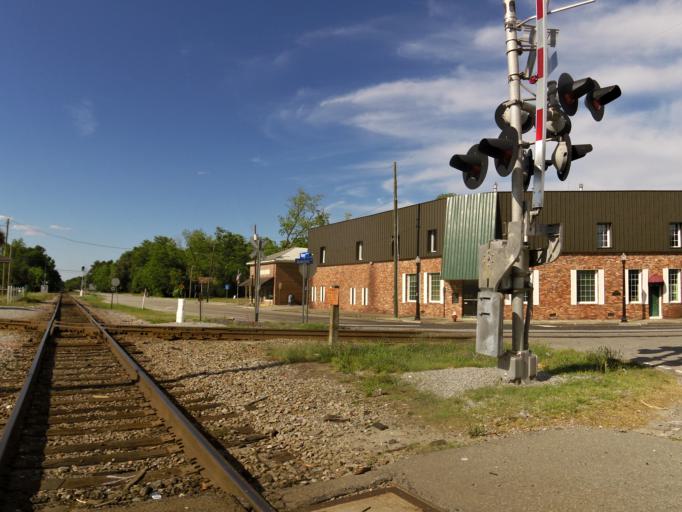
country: US
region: South Carolina
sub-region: Allendale County
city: Fairfax
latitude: 32.9588
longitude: -81.2369
